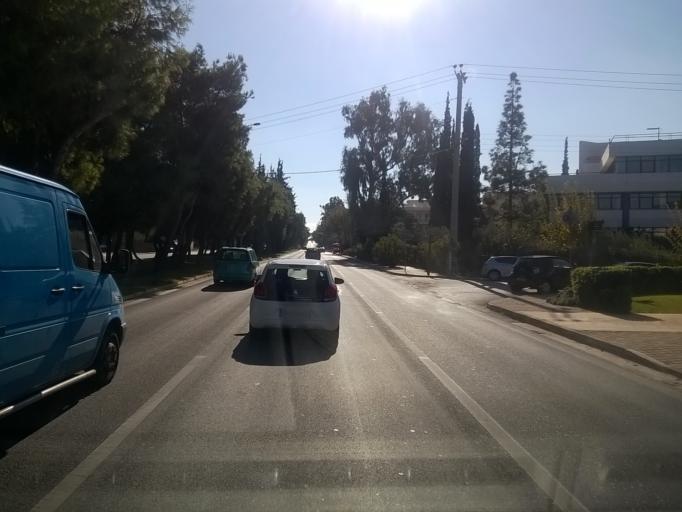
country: GR
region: Attica
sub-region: Nomarchia Anatolikis Attikis
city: Voula
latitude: 37.8292
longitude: 23.7735
